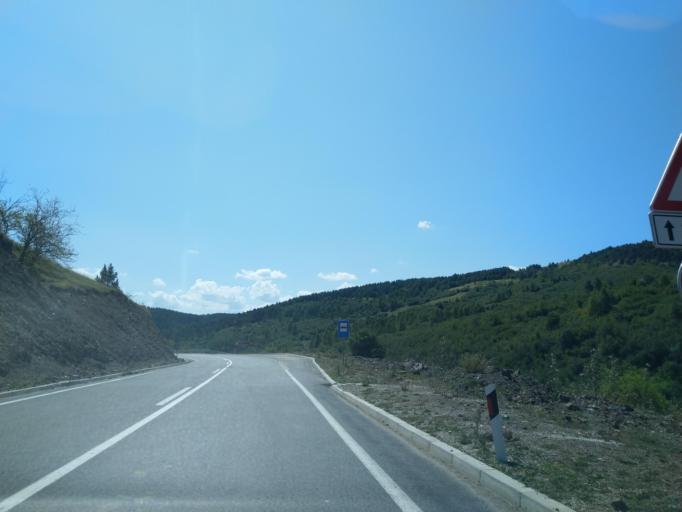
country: RS
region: Central Serbia
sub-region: Zlatiborski Okrug
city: Sjenica
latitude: 43.2874
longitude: 19.9435
